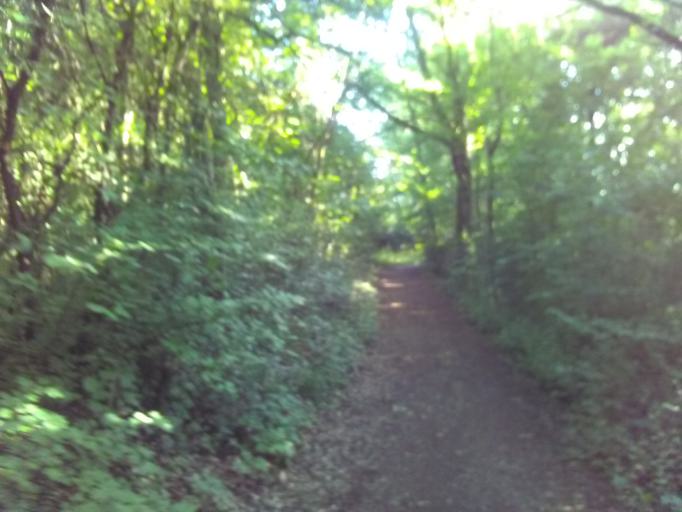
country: DE
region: Bavaria
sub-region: Upper Franconia
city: Stegaurach
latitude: 49.8790
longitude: 10.8719
